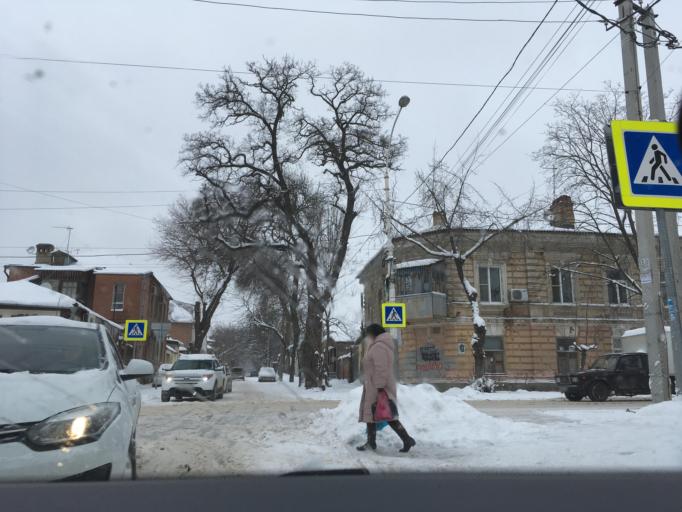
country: RU
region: Rostov
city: Rostov-na-Donu
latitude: 47.2306
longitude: 39.7540
